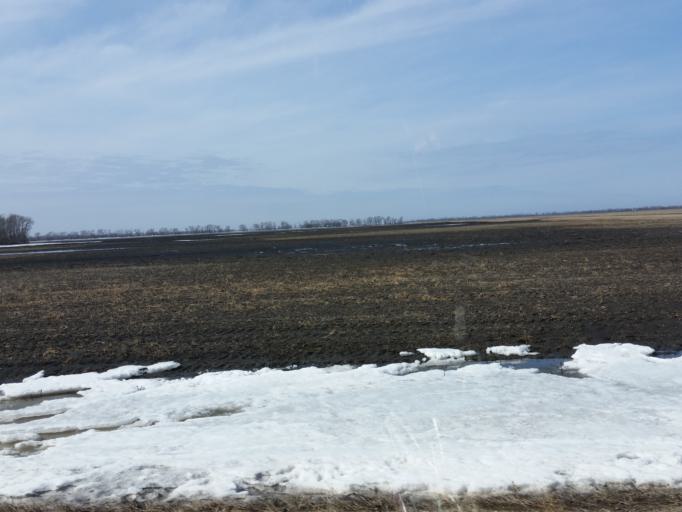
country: US
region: North Dakota
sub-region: Walsh County
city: Grafton
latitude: 48.3093
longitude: -97.2111
